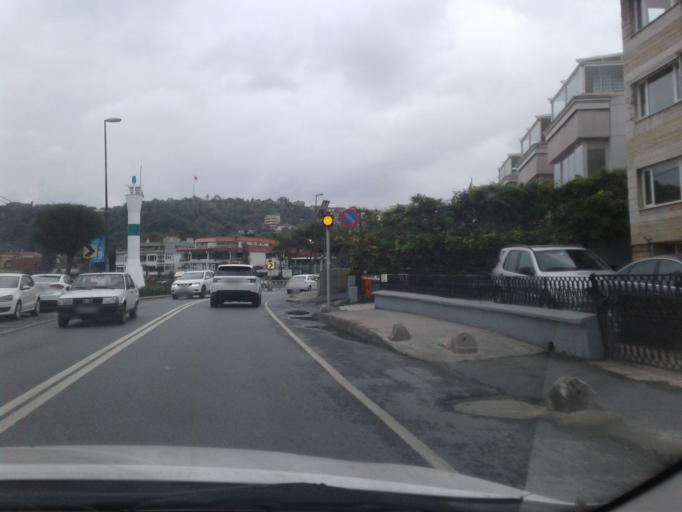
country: TR
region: Istanbul
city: Sisli
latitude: 41.0998
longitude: 29.0545
